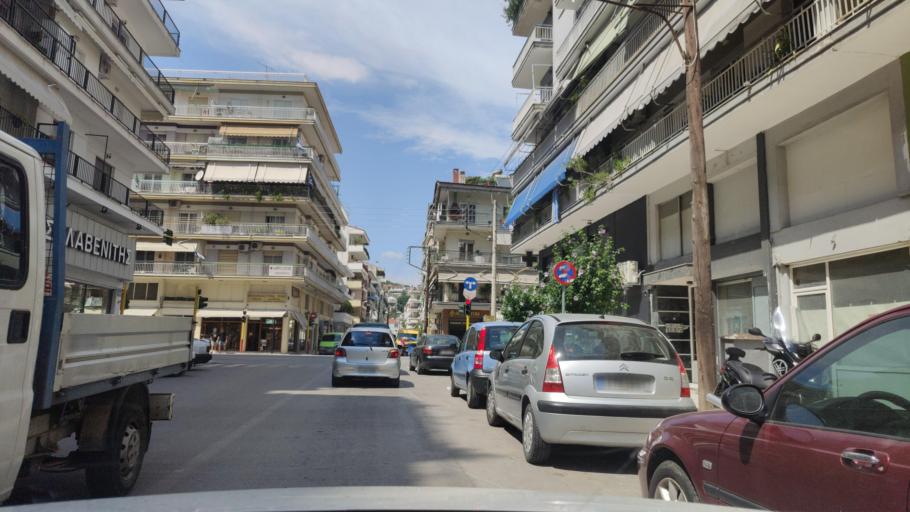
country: GR
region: Central Macedonia
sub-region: Nomos Serron
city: Serres
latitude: 41.0873
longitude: 23.5411
